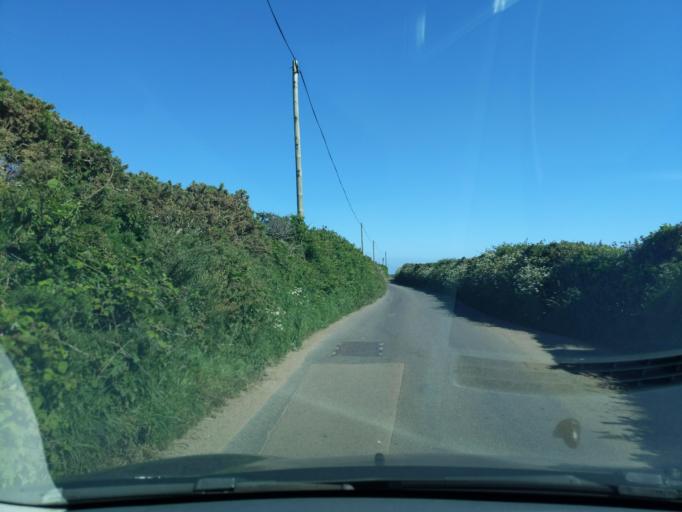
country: GB
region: England
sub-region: Cornwall
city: St. Buryan
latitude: 50.0675
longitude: -5.6061
